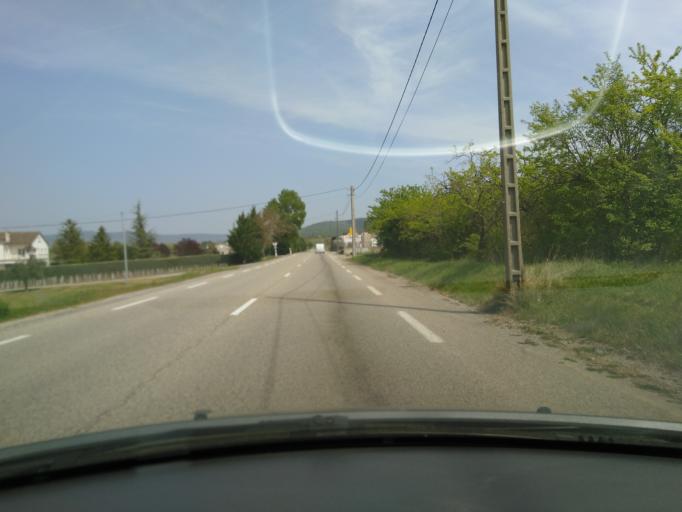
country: FR
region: Rhone-Alpes
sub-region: Departement de l'Ardeche
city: Saint-Sernin
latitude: 44.5264
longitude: 4.4115
